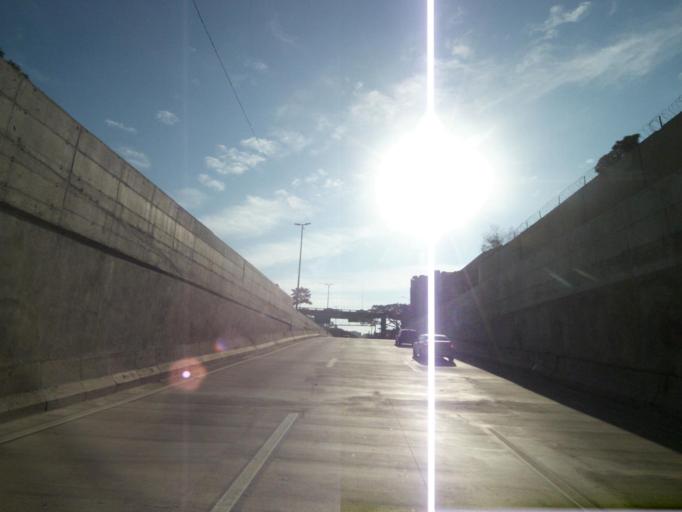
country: BR
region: Rio de Janeiro
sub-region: Niteroi
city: Niteroi
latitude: -22.8825
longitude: -43.1142
